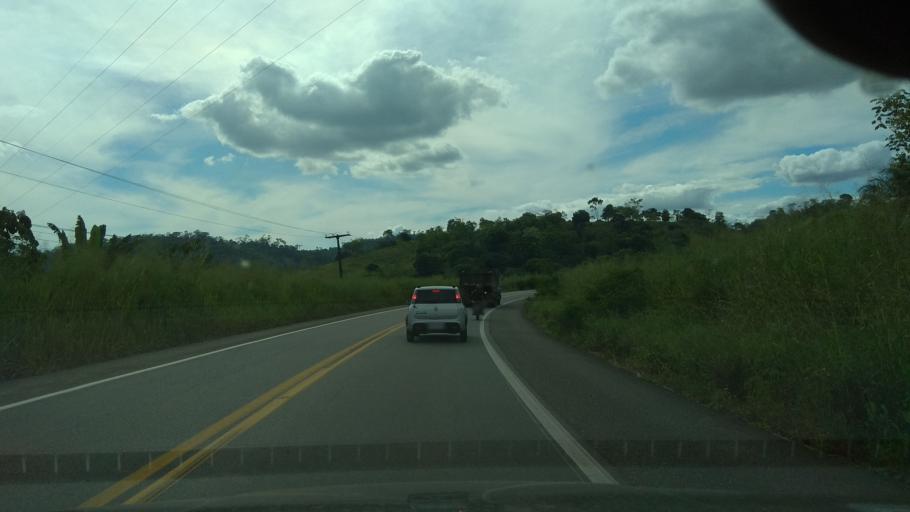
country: BR
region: Bahia
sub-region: Ipiau
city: Ipiau
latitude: -14.1043
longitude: -39.7770
